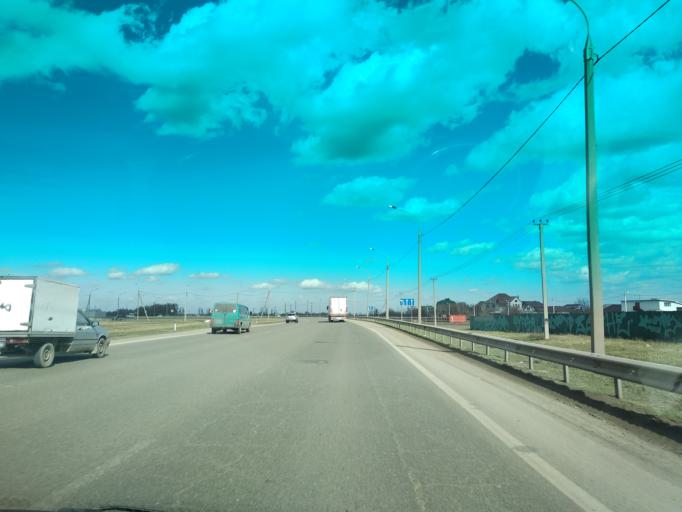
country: RU
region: Krasnodarskiy
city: Pashkovskiy
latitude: 45.0623
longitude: 39.1346
